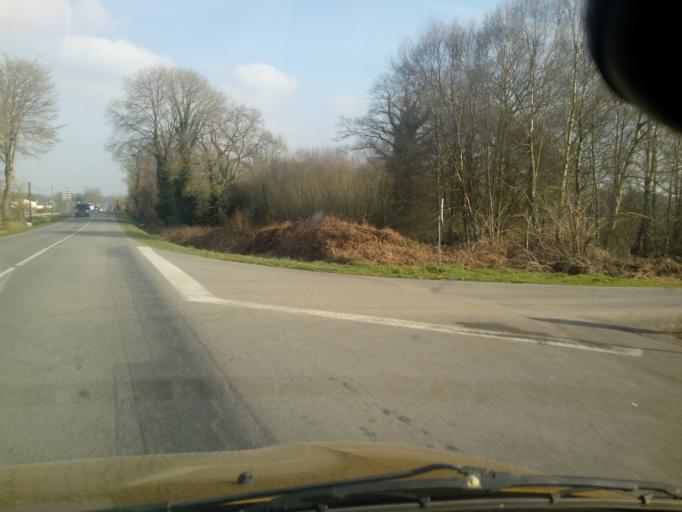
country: FR
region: Brittany
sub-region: Departement du Morbihan
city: La Vraie-Croix
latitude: 47.6960
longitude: -2.5057
